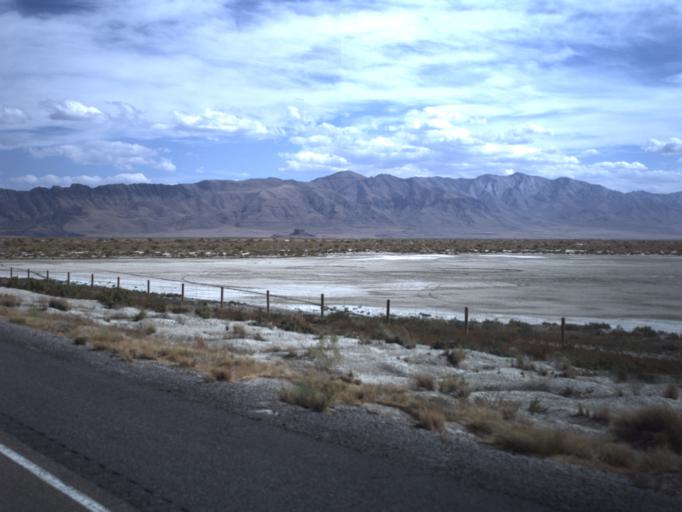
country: US
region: Utah
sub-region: Tooele County
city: Grantsville
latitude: 40.7555
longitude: -112.7519
